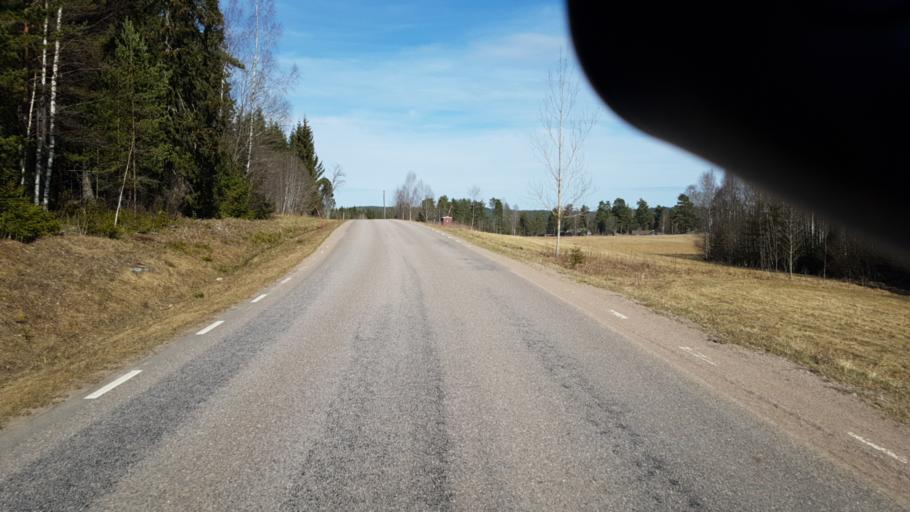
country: SE
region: Vaermland
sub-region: Arvika Kommun
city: Arvika
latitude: 59.6216
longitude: 12.7933
